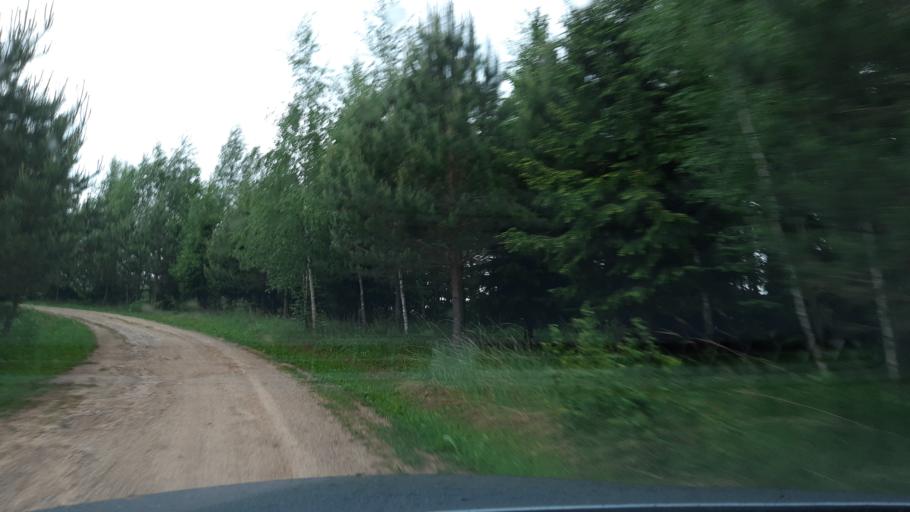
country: LT
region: Utenos apskritis
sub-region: Anyksciai
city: Anyksciai
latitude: 55.4461
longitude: 25.1961
